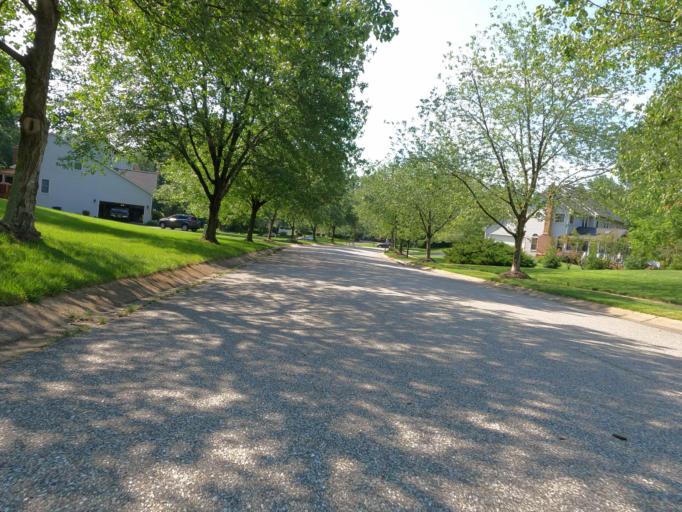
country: US
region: Maryland
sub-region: Anne Arundel County
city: Pasadena
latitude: 39.1034
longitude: -76.5758
